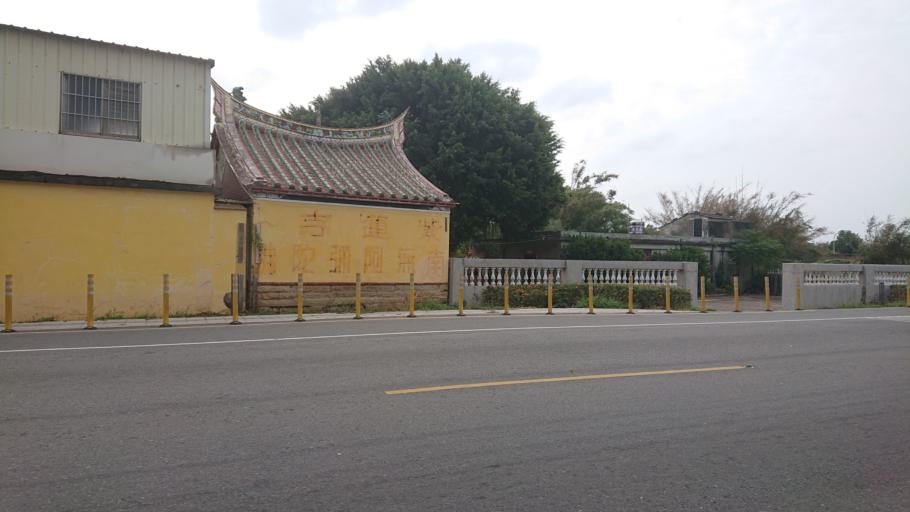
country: TW
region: Fukien
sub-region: Kinmen
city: Jincheng
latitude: 24.4340
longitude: 118.3262
